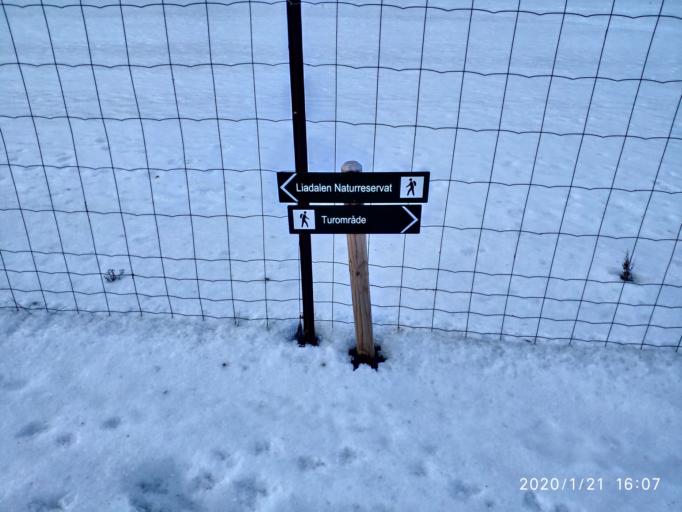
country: NO
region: Oppland
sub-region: Nord-Fron
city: Vinstra
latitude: 61.5919
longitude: 9.7211
